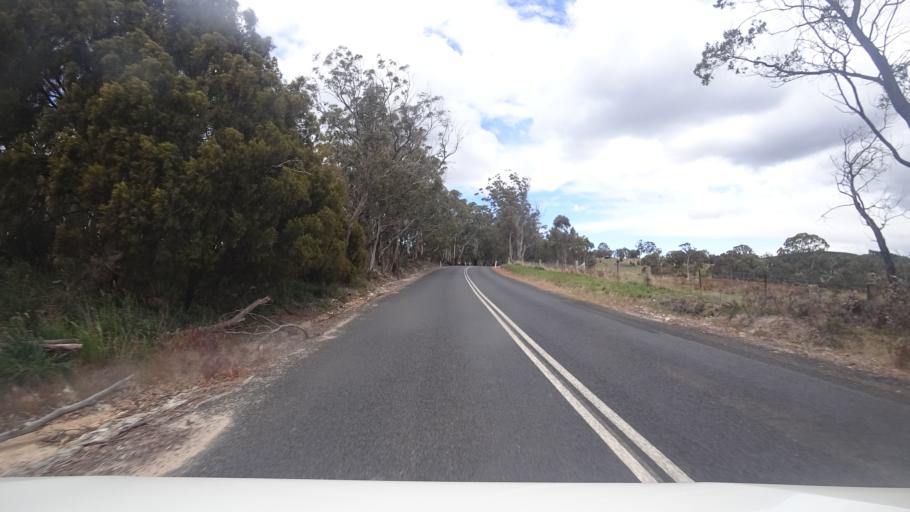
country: AU
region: New South Wales
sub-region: Oberon
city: Oberon
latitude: -33.6272
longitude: 149.8927
